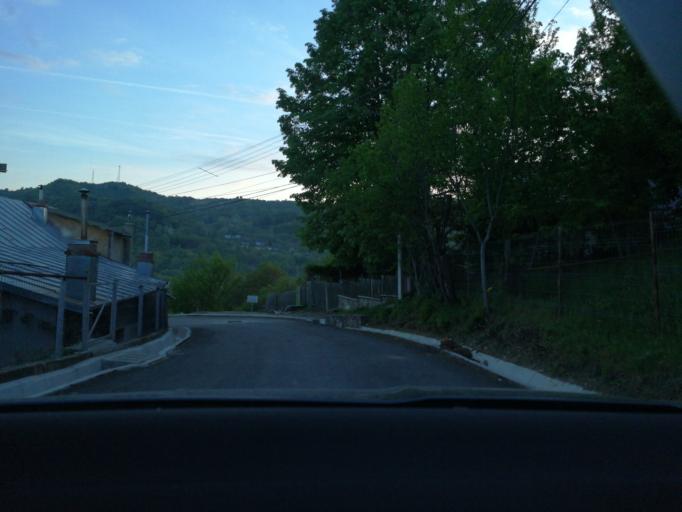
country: RO
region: Prahova
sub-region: Comuna Cornu
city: Cornu de Jos
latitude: 45.1440
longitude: 25.7052
